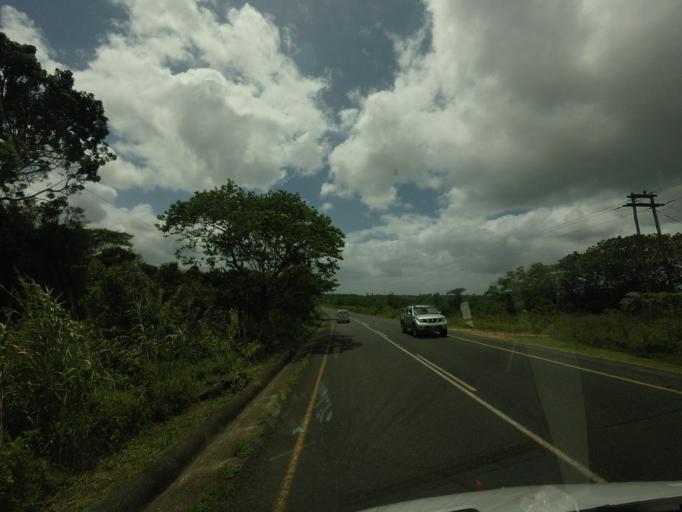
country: ZA
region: KwaZulu-Natal
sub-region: uMkhanyakude District Municipality
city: Mtubatuba
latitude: -28.3735
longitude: 32.3965
